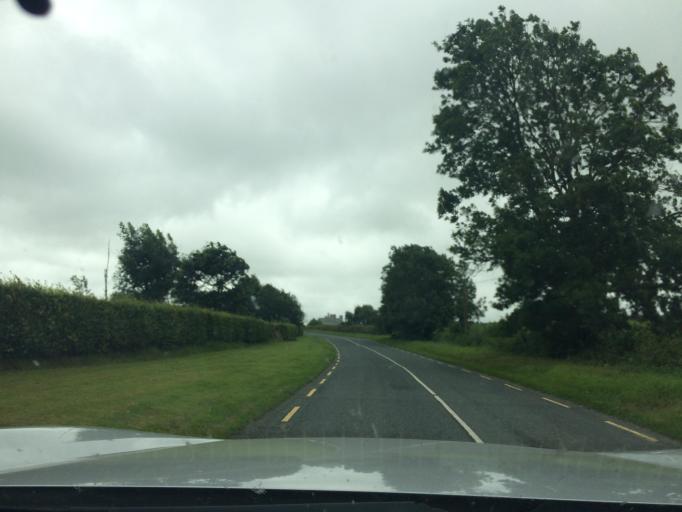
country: IE
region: Munster
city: Cashel
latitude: 52.5337
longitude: -7.8901
